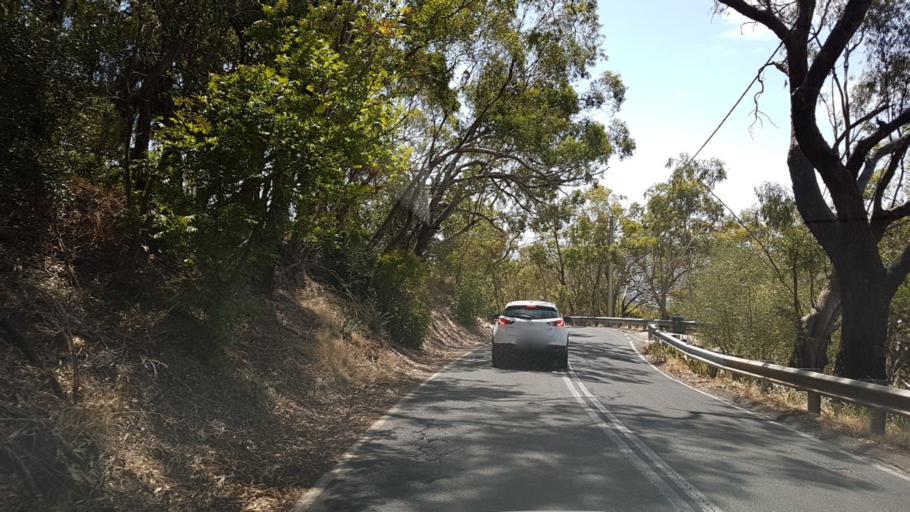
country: AU
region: South Australia
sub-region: Mitcham
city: Belair
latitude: -34.9938
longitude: 138.6281
